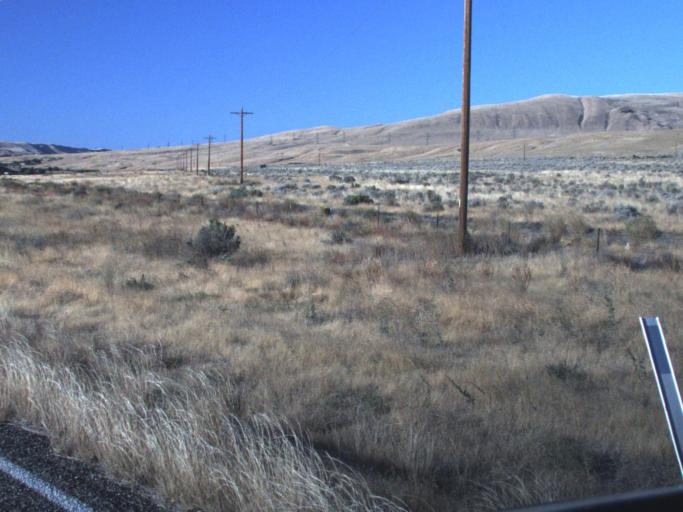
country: US
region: Washington
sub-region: Benton County
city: Benton City
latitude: 46.3583
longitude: -119.4523
